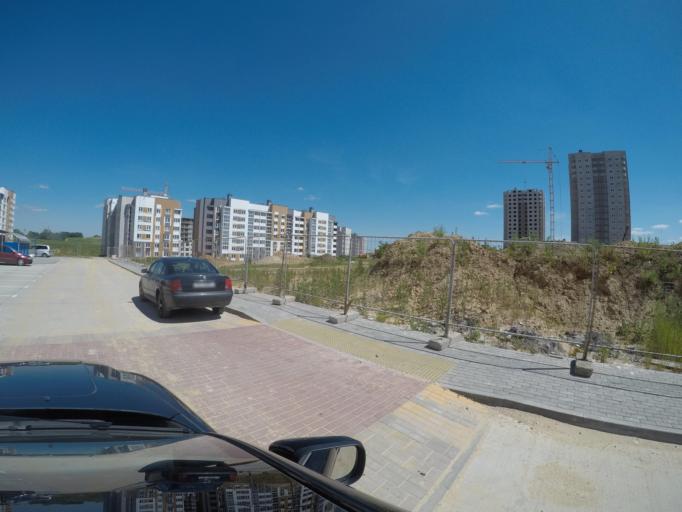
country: BY
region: Grodnenskaya
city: Hrodna
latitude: 53.7203
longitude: 23.8809
